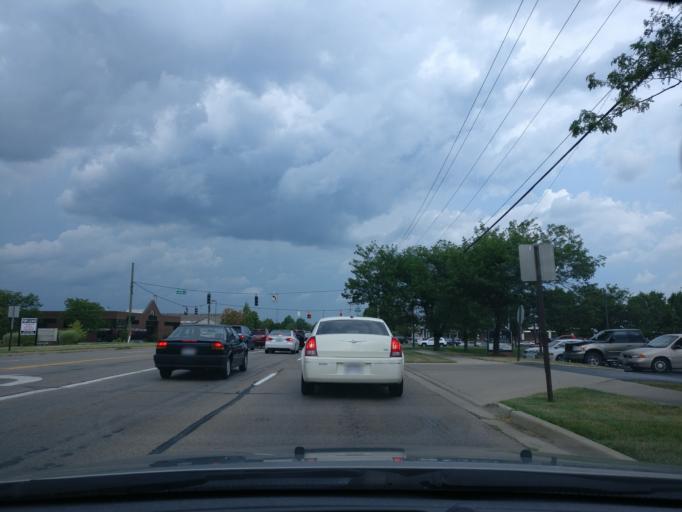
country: US
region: Ohio
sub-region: Montgomery County
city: Centerville
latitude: 39.6250
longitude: -84.1996
